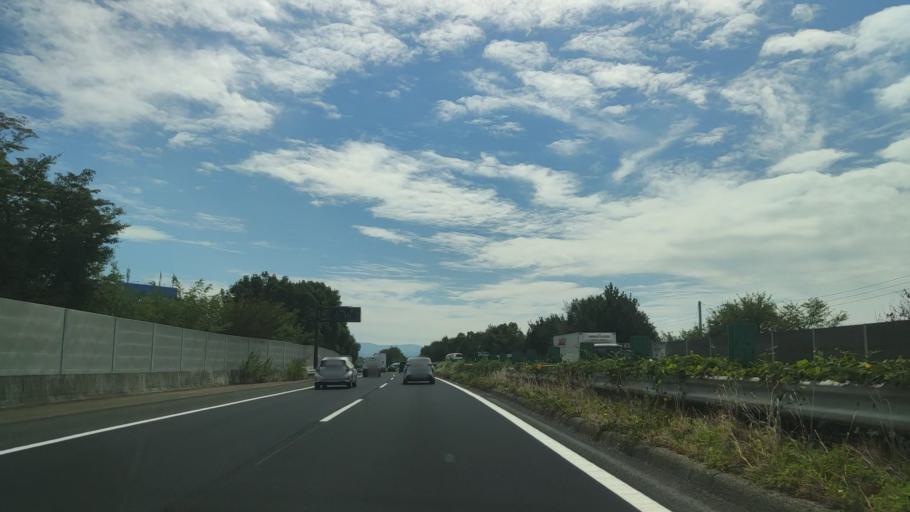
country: JP
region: Aichi
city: Okazaki
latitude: 34.9730
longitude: 137.1836
